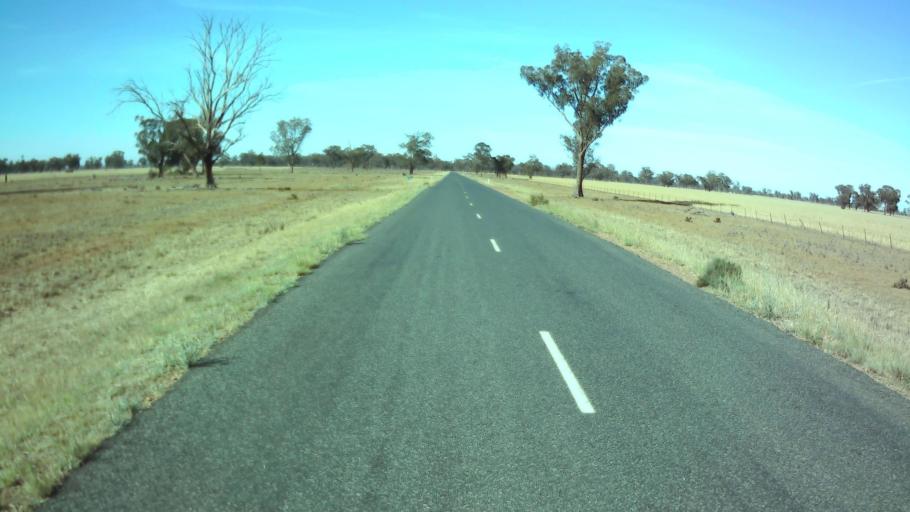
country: AU
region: New South Wales
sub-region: Weddin
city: Grenfell
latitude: -34.0524
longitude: 147.9177
